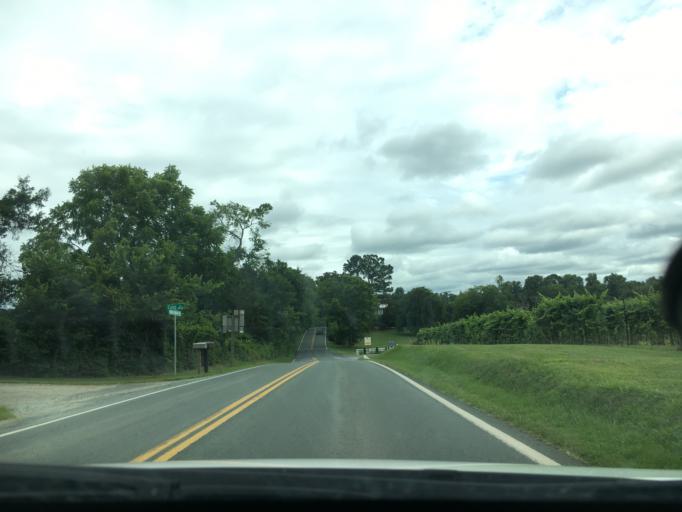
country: US
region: Virginia
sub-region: City of Charlottesville
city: Charlottesville
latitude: 37.9926
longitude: -78.4445
